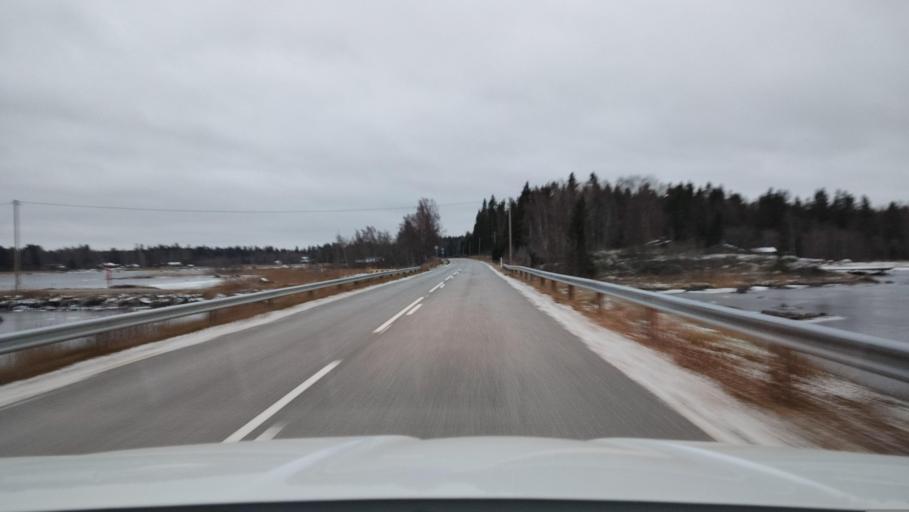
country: FI
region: Ostrobothnia
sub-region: Vaasa
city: Replot
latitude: 63.2715
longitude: 21.3443
